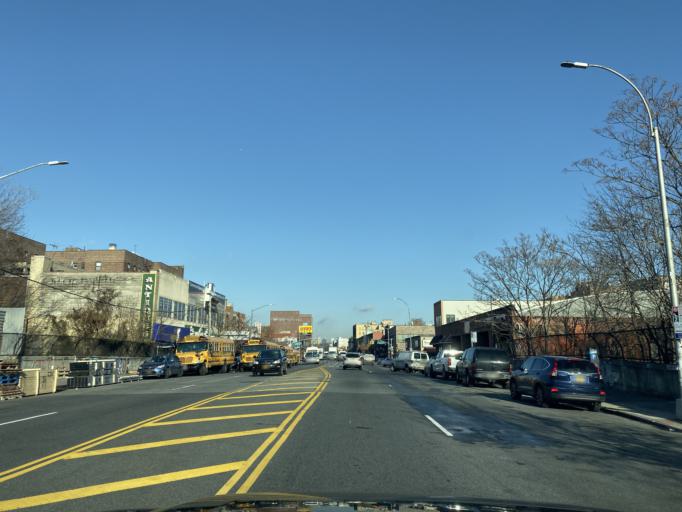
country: US
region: New York
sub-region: Kings County
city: Brooklyn
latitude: 40.6284
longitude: -73.9658
